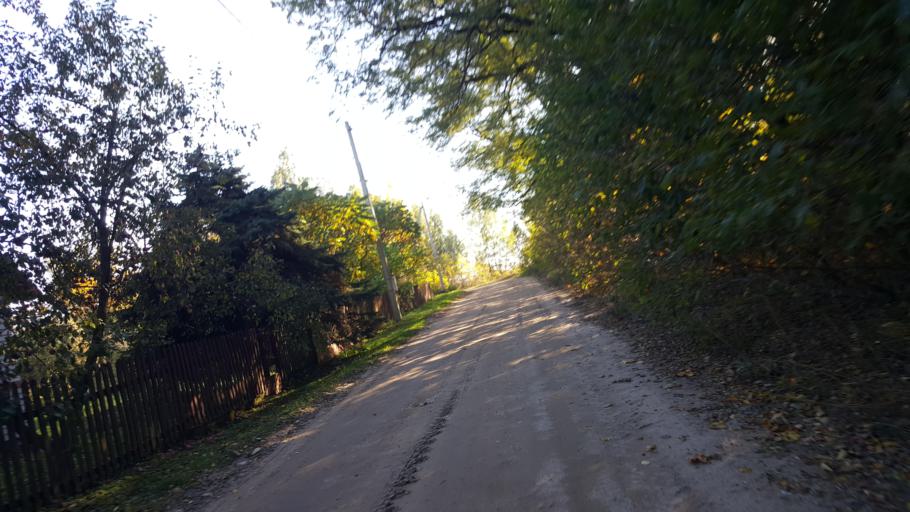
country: BY
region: Brest
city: Kamyanyets
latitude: 52.3901
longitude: 23.8842
